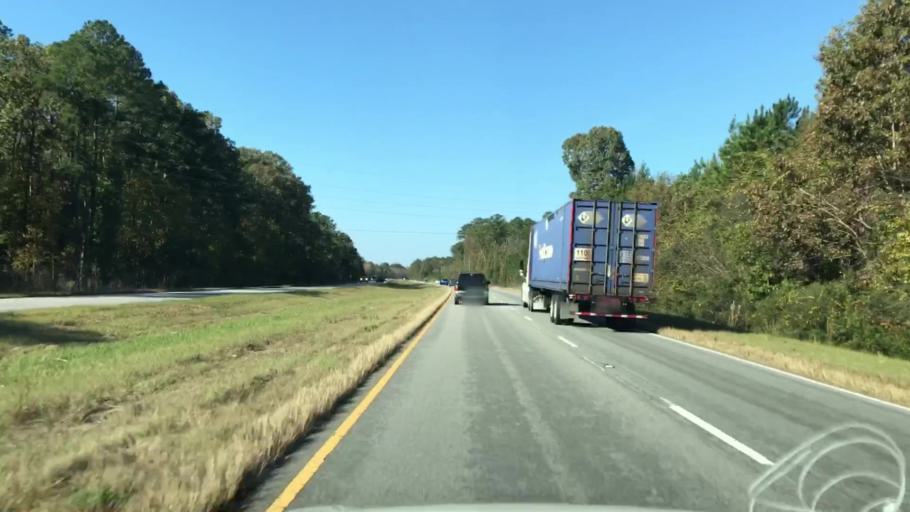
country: US
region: South Carolina
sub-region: Charleston County
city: Ravenel
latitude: 32.7627
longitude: -80.4266
